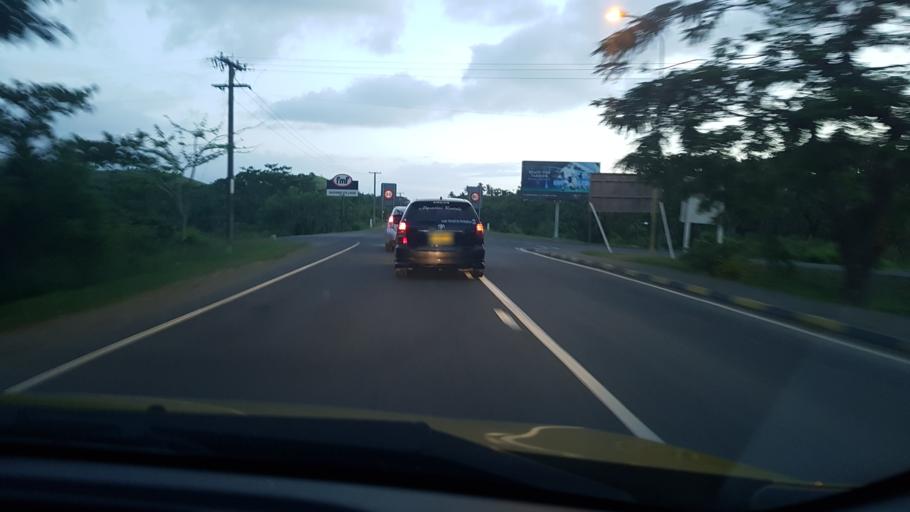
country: FJ
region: Western
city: Nadi
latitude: -18.1453
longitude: 177.5126
